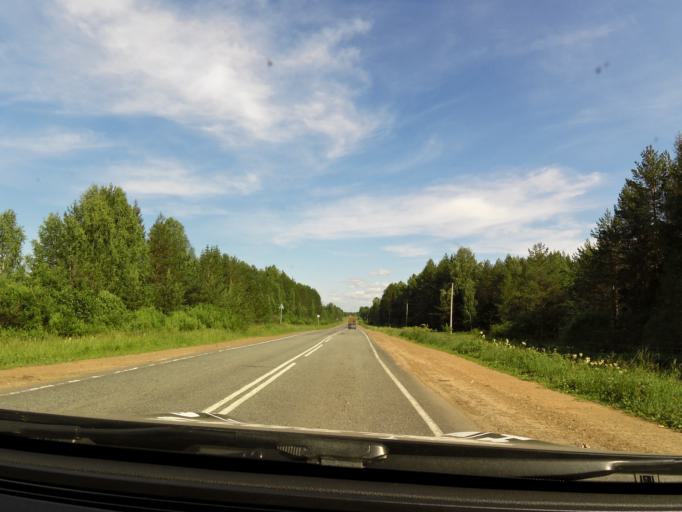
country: RU
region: Kirov
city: Belaya Kholunitsa
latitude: 58.8528
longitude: 50.7327
